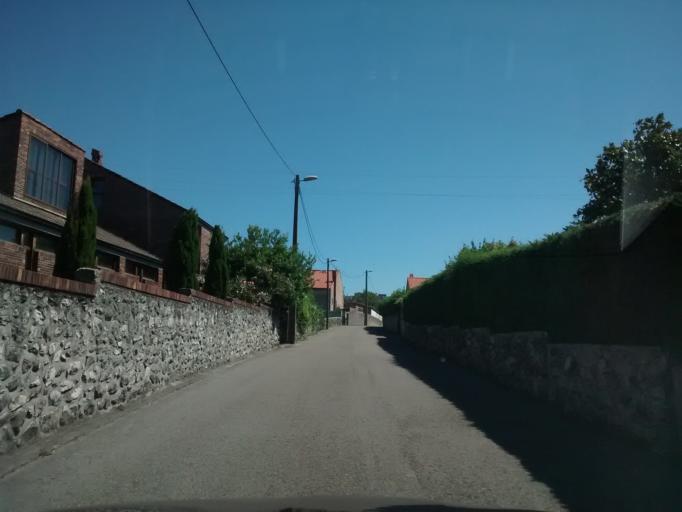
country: ES
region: Cantabria
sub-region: Provincia de Cantabria
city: Santander
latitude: 43.4704
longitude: -3.8304
